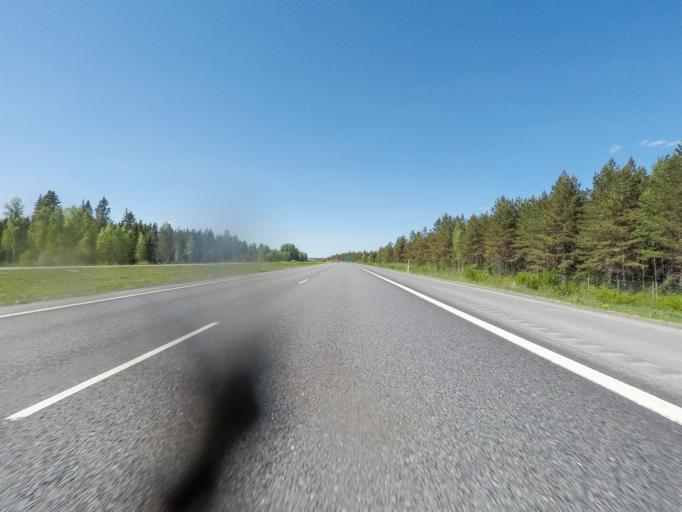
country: FI
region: Haeme
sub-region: Haemeenlinna
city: Kalvola
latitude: 61.1326
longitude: 24.0987
